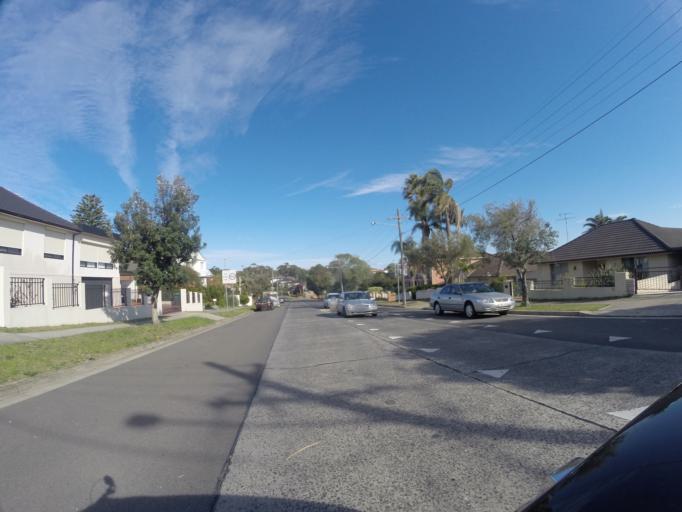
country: AU
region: New South Wales
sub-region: Randwick
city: South Coogee
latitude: -33.9342
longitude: 151.2533
